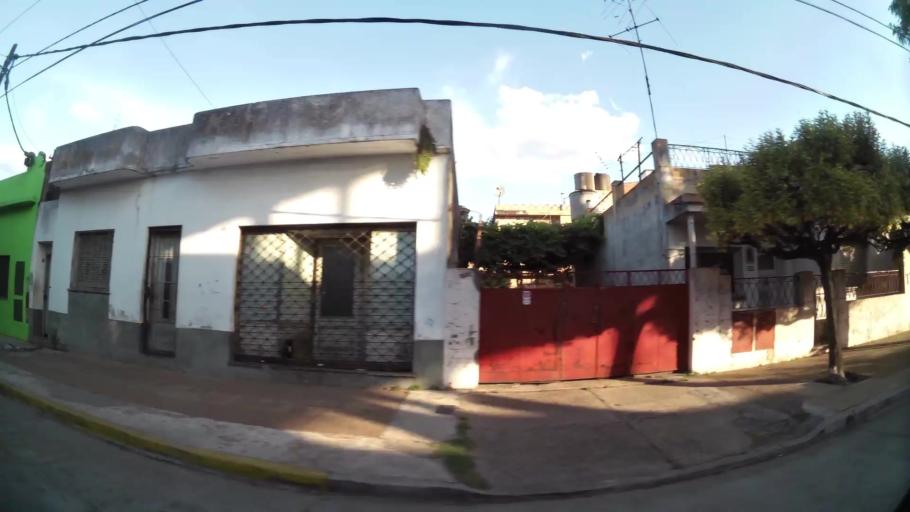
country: AR
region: Buenos Aires F.D.
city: Villa Lugano
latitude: -34.6930
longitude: -58.4856
